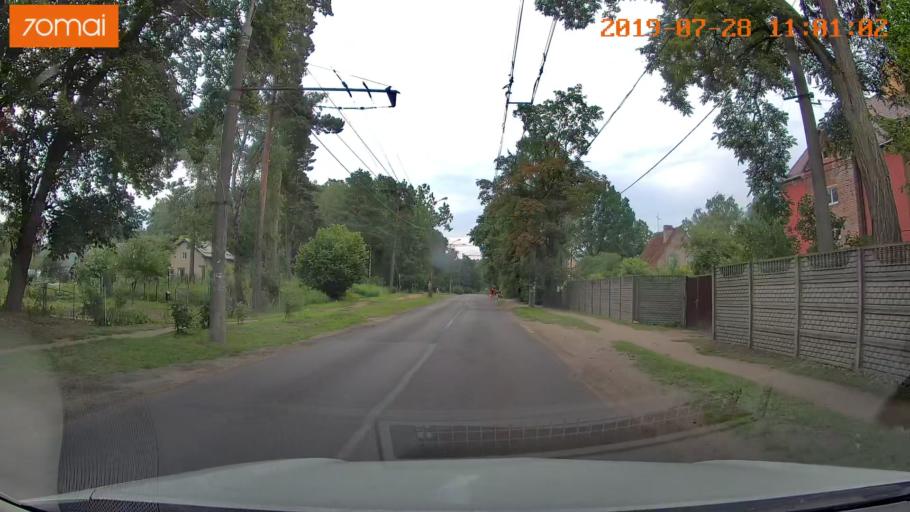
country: RU
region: Kaliningrad
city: Vzmorye
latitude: 54.7239
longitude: 20.3656
